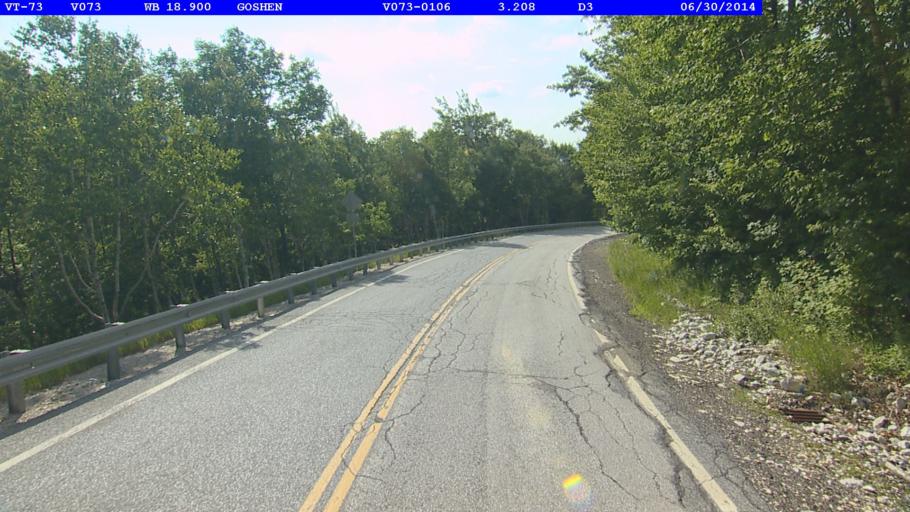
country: US
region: Vermont
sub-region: Rutland County
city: Brandon
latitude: 43.8405
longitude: -72.9718
